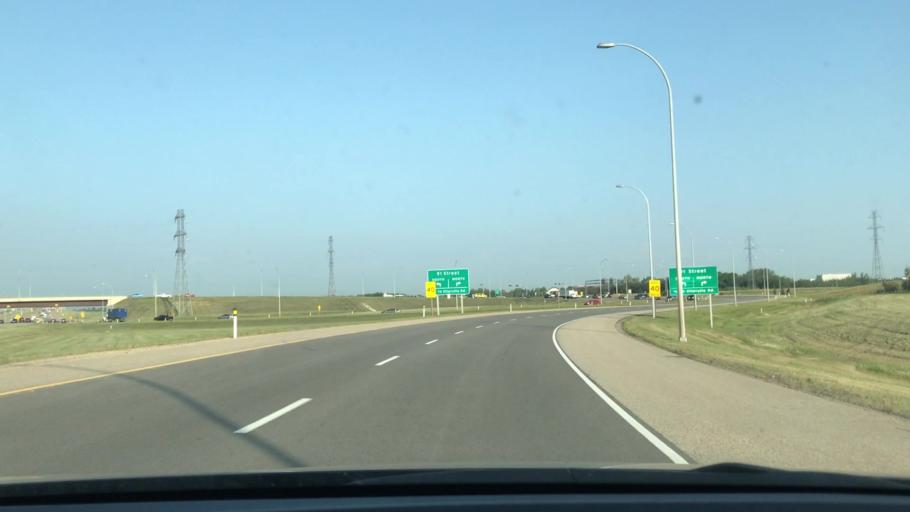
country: CA
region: Alberta
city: Beaumont
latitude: 53.4376
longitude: -113.4608
